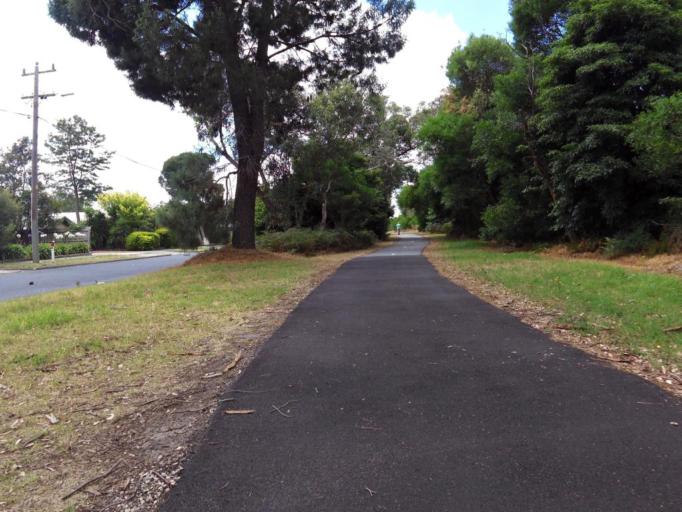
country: AU
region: Victoria
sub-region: Frankston
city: Frankston South
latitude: -38.1564
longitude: 145.1490
